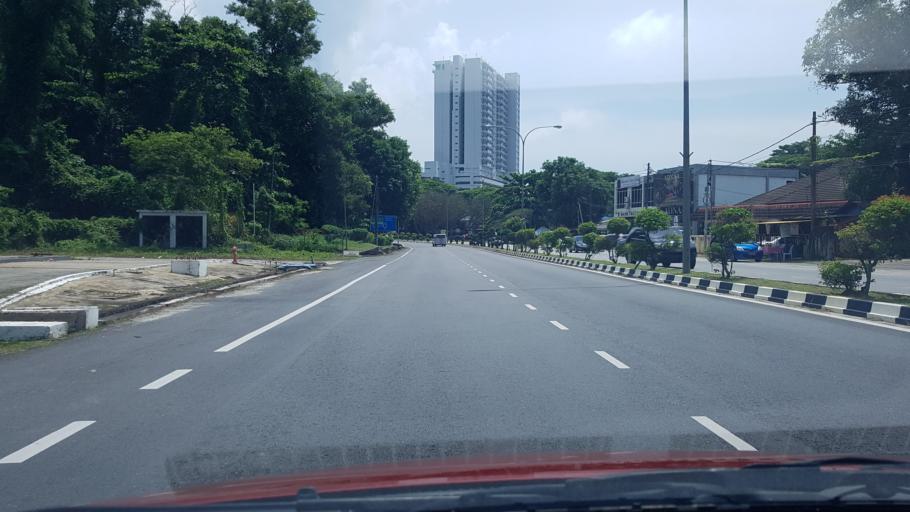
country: MY
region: Terengganu
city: Kuala Terengganu
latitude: 5.3188
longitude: 103.1436
